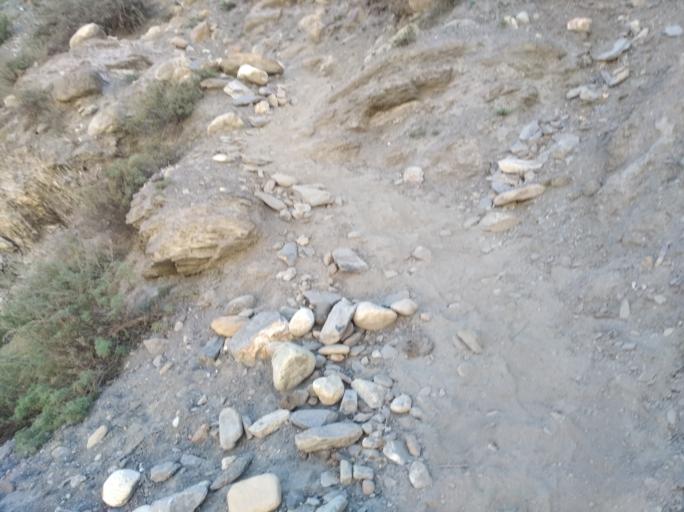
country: NP
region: Western Region
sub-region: Dhawalagiri Zone
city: Jomsom
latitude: 28.8635
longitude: 83.3424
